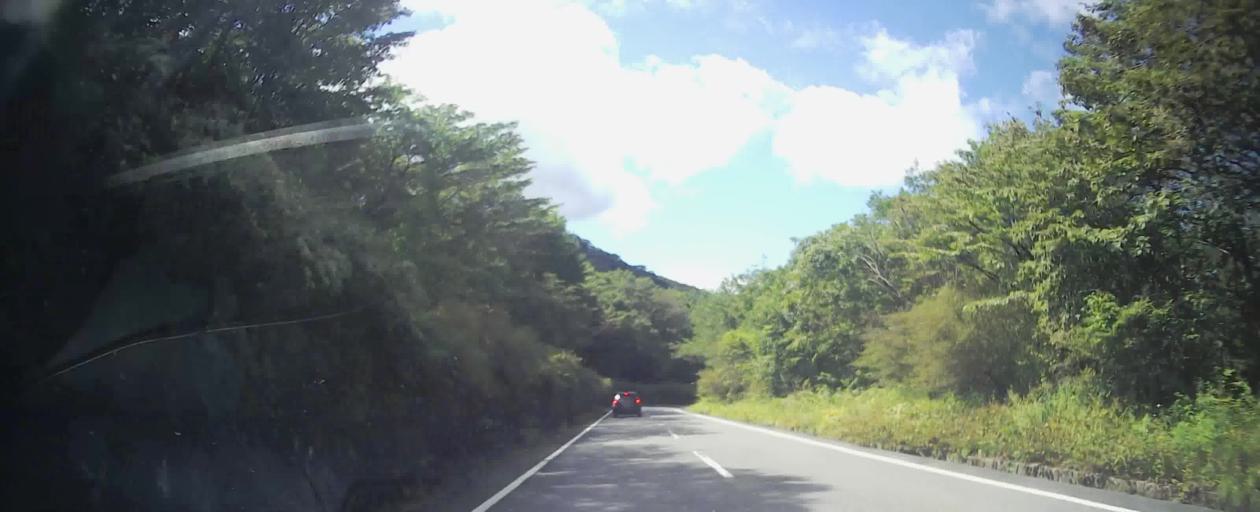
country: JP
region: Gunma
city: Shibukawa
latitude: 36.4685
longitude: 138.8851
